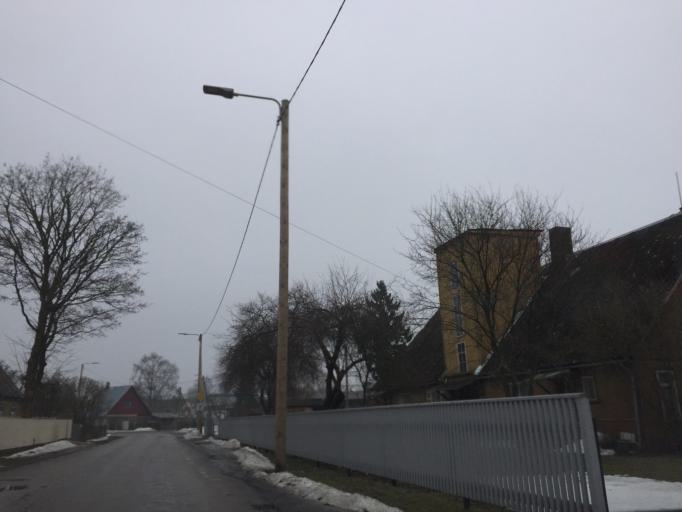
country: EE
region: Saare
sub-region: Kuressaare linn
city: Kuressaare
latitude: 58.2478
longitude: 22.4887
